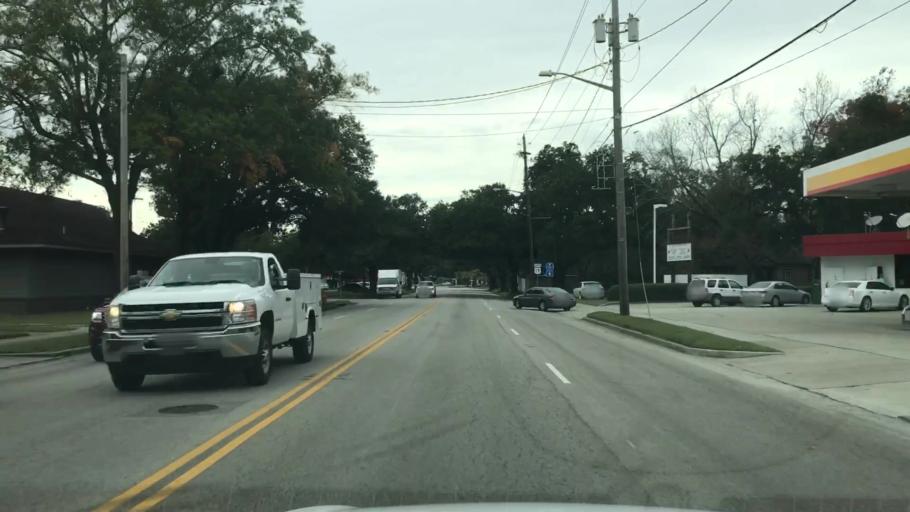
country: US
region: South Carolina
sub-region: Georgetown County
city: Georgetown
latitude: 33.3739
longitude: -79.2834
